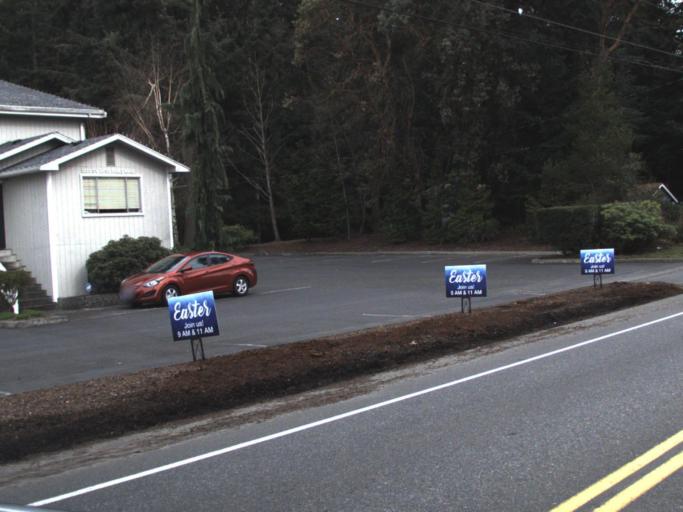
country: US
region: Washington
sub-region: King County
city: Federal Way
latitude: 47.3275
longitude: -122.3508
